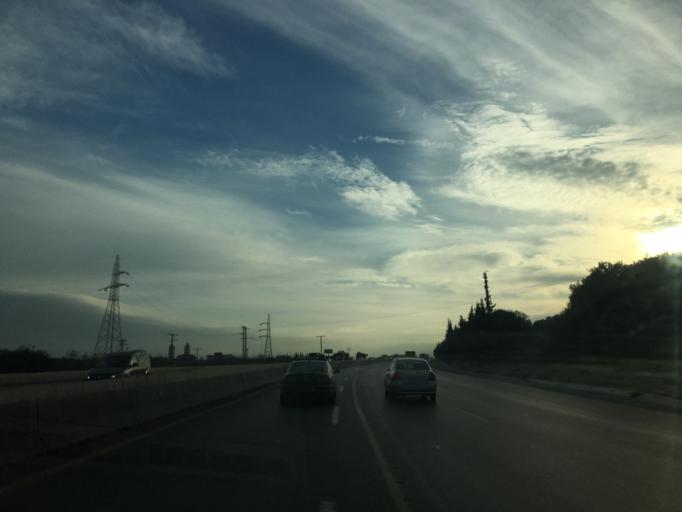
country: DZ
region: Bouira
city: Draa el Mizan
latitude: 36.4753
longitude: 3.7509
